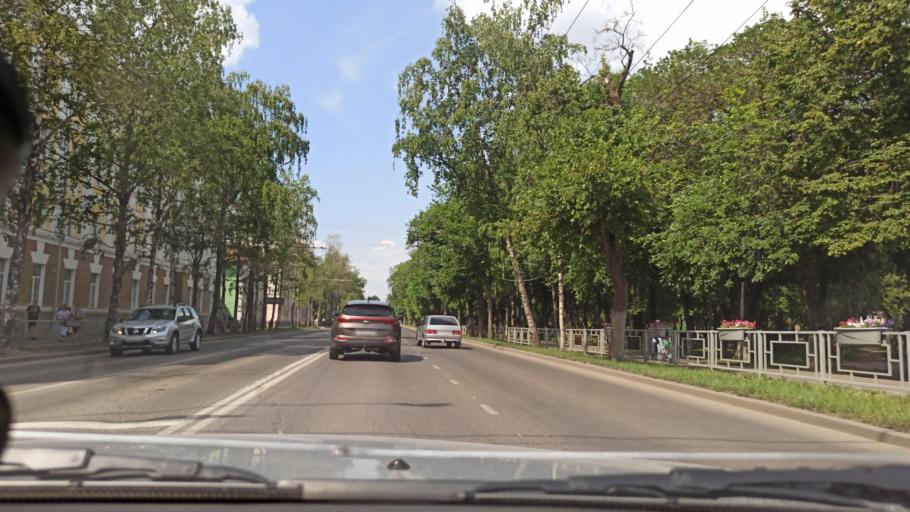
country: RU
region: Vologda
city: Vologda
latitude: 59.2194
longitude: 39.8778
